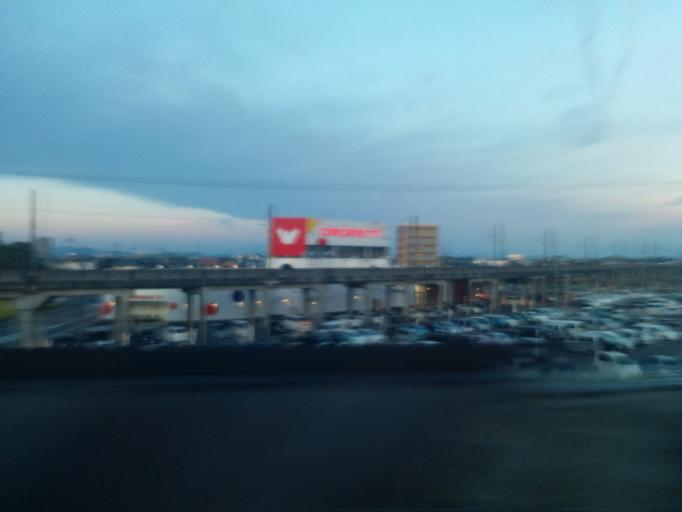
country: JP
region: Aichi
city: Sobue
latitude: 35.3136
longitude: 136.6882
